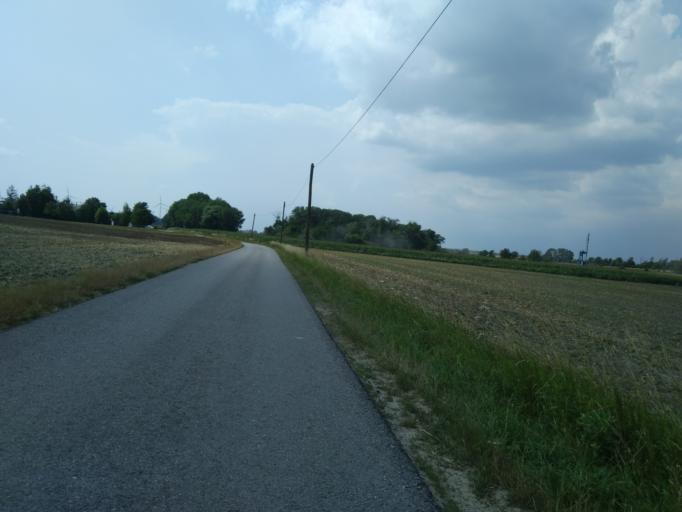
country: AT
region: Lower Austria
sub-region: Politischer Bezirk Ganserndorf
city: Ganserndorf
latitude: 48.3566
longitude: 16.7041
